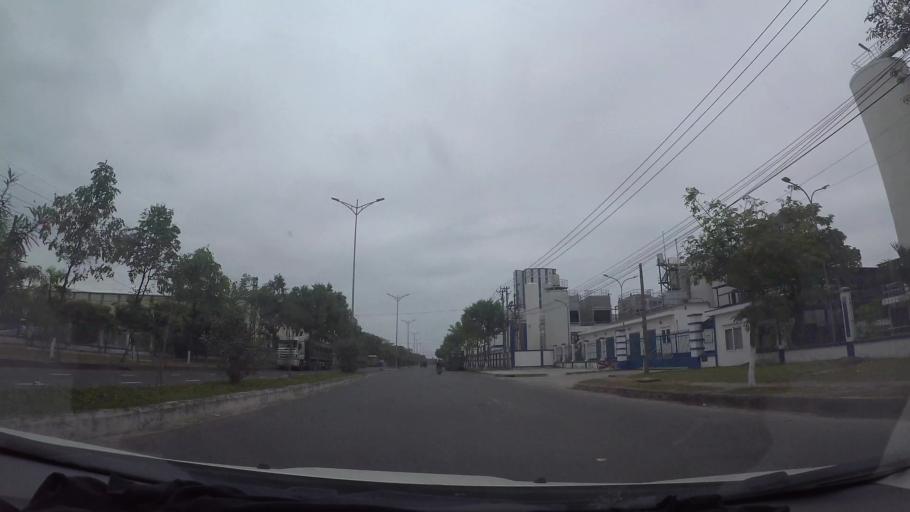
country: VN
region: Da Nang
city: Lien Chieu
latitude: 16.0793
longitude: 108.1417
